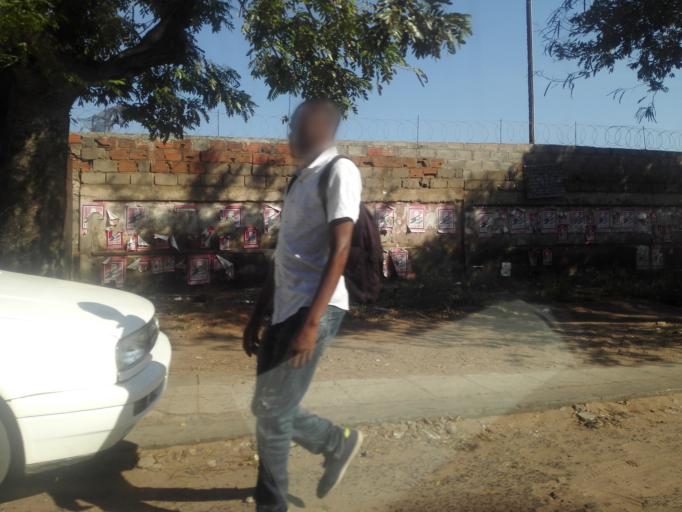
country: MZ
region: Maputo City
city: Maputo
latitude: -25.9582
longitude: 32.5850
